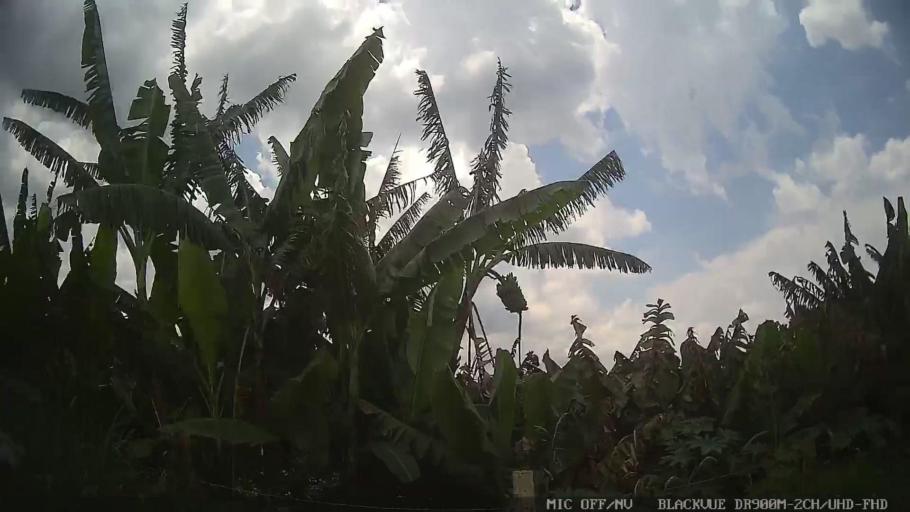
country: BR
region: Sao Paulo
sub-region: Ferraz De Vasconcelos
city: Ferraz de Vasconcelos
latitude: -23.6141
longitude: -46.3780
